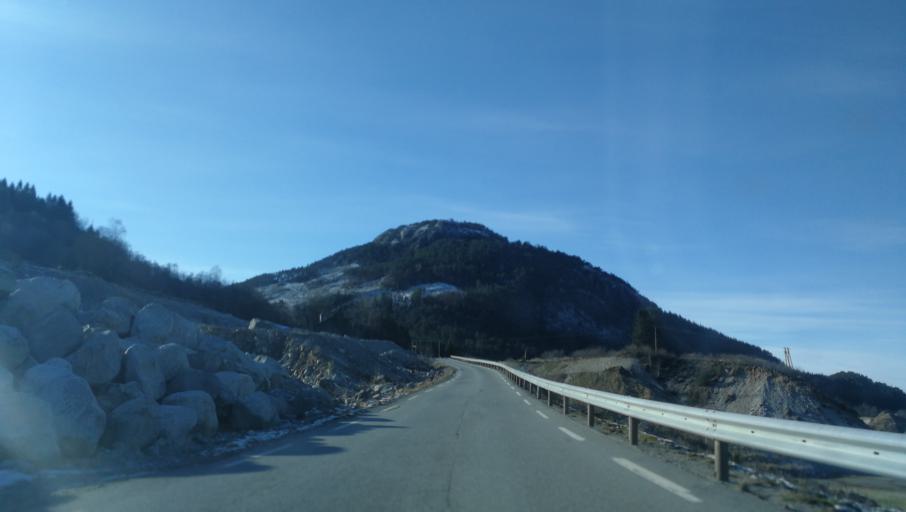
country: NO
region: Rogaland
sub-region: Hjelmeland
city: Hjelmelandsvagen
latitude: 59.1286
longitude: 6.2620
